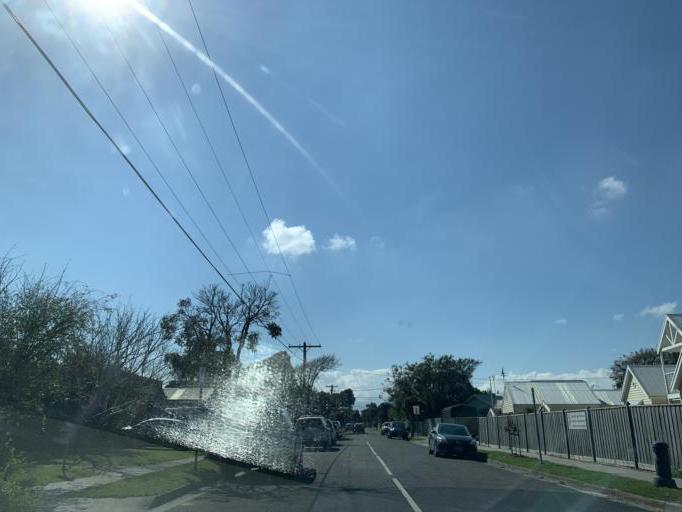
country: AU
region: Victoria
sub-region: Kingston
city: Aspendale
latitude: -38.0197
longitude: 145.0988
